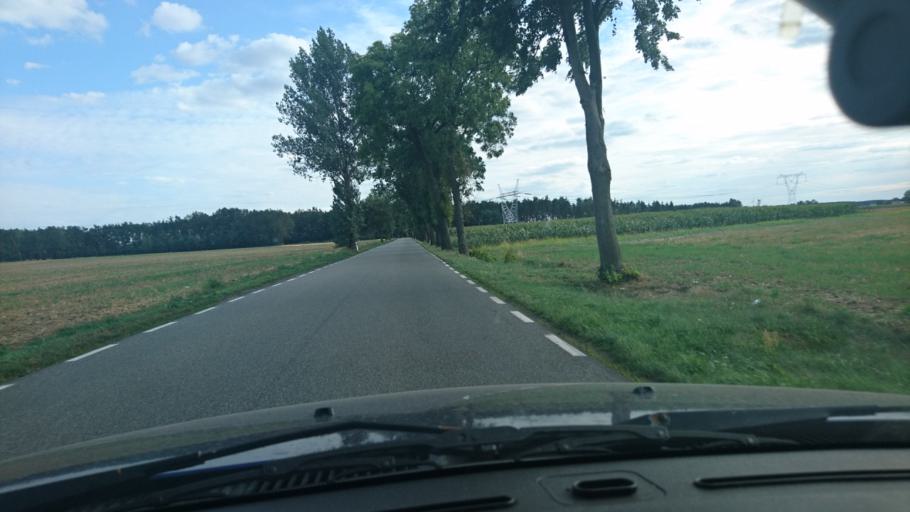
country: PL
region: Greater Poland Voivodeship
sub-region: Powiat ostrowski
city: Odolanow
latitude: 51.5554
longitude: 17.6990
